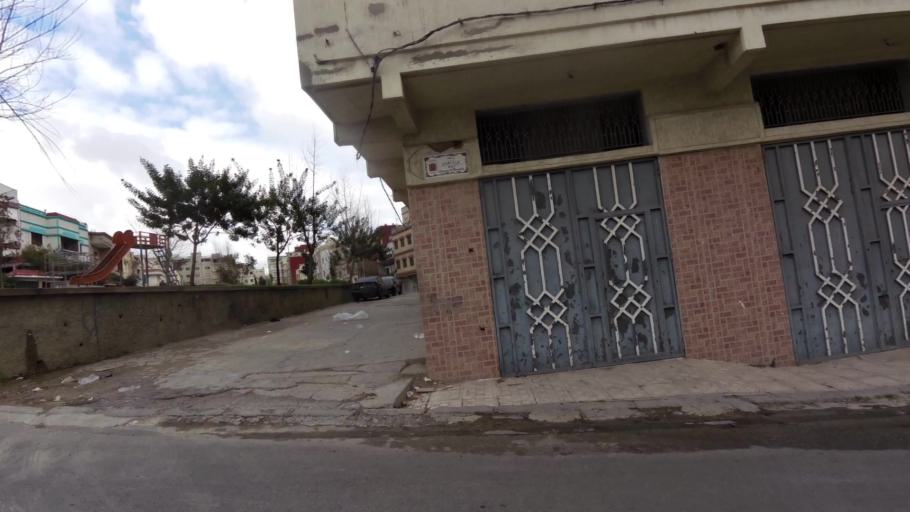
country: MA
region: Tanger-Tetouan
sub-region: Tanger-Assilah
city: Tangier
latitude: 35.7632
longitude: -5.8018
